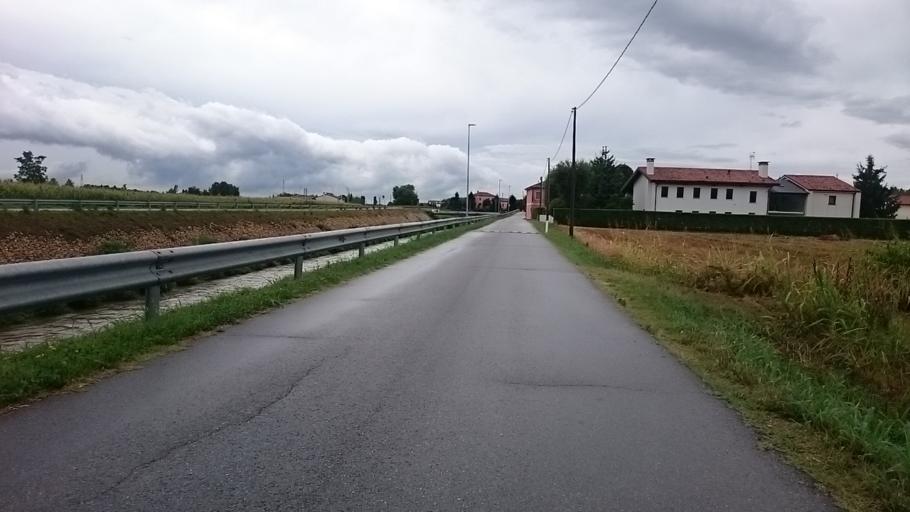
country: IT
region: Veneto
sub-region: Provincia di Treviso
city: Sant'Andrea
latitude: 45.6478
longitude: 11.9221
